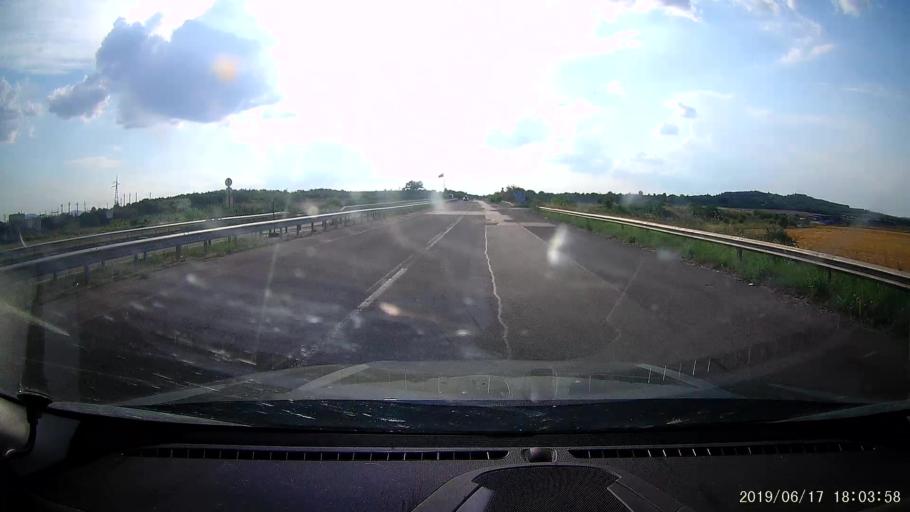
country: BG
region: Khaskovo
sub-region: Obshtina Svilengrad
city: Svilengrad
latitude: 41.7823
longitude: 26.2088
